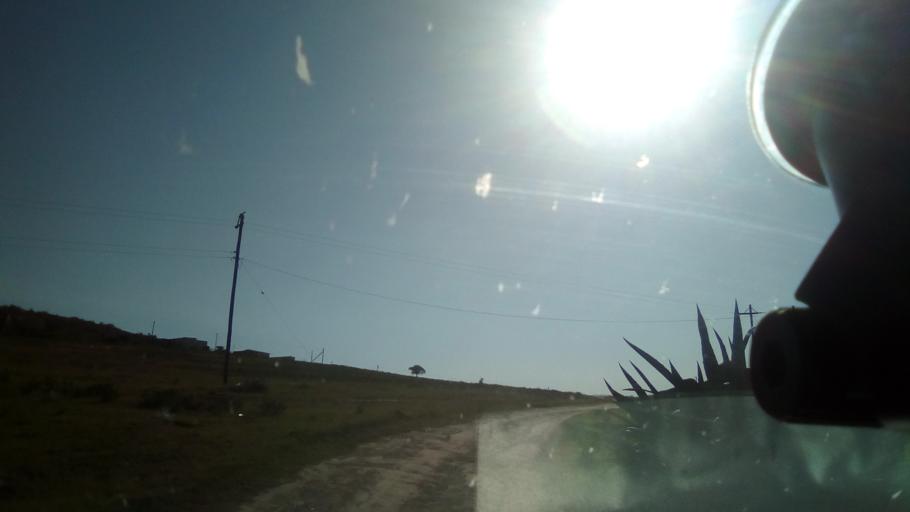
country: ZA
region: Eastern Cape
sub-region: Buffalo City Metropolitan Municipality
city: Bhisho
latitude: -32.8095
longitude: 27.3575
